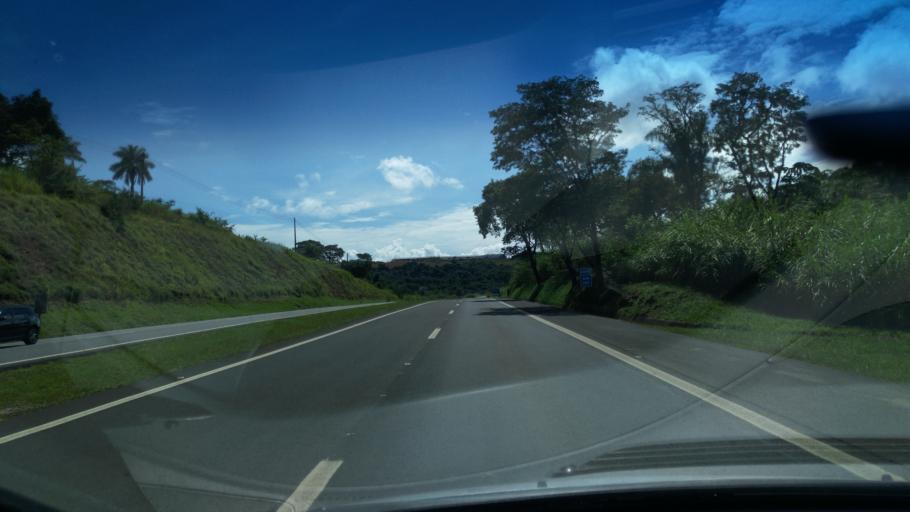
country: BR
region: Sao Paulo
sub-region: Santo Antonio Do Jardim
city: Espirito Santo do Pinhal
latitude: -22.2157
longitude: -46.7855
